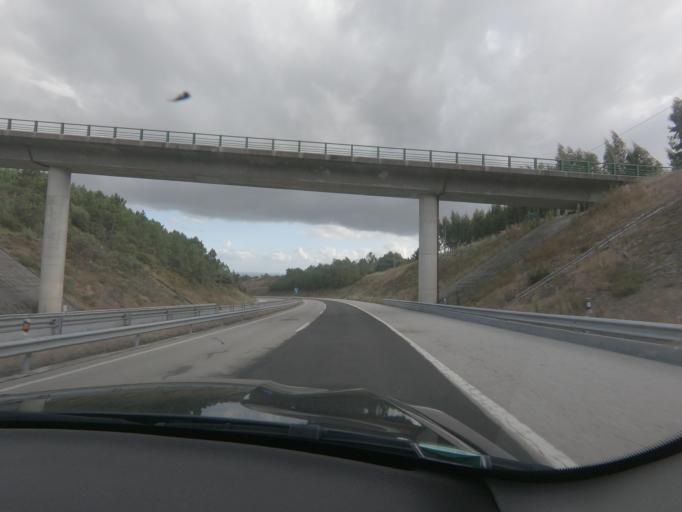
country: PT
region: Viseu
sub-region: Castro Daire
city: Castro Daire
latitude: 40.9247
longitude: -7.9179
